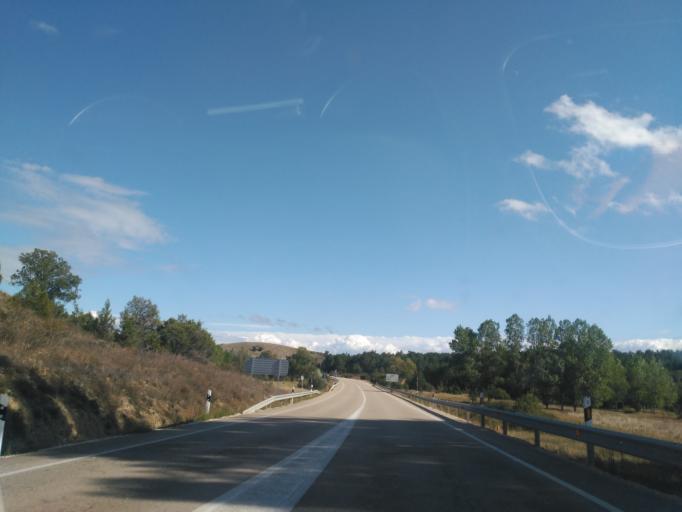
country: ES
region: Castille and Leon
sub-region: Provincia de Burgos
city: Rabanera del Pinar
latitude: 41.8811
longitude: -3.2271
